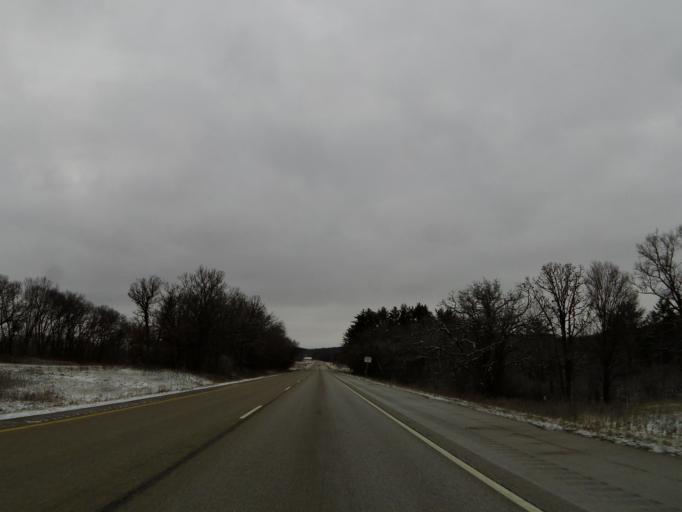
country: US
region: Wisconsin
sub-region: Trempealeau County
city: Osseo
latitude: 44.5383
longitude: -91.1568
